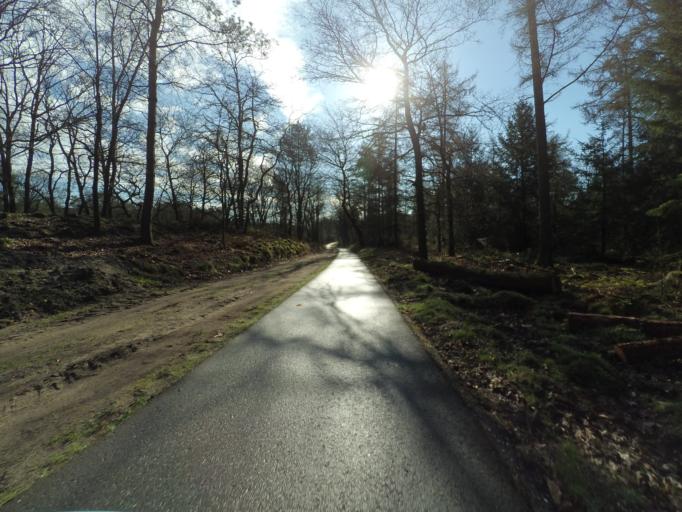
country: NL
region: Gelderland
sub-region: Gemeente Apeldoorn
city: Beekbergen
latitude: 52.1934
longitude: 5.8783
